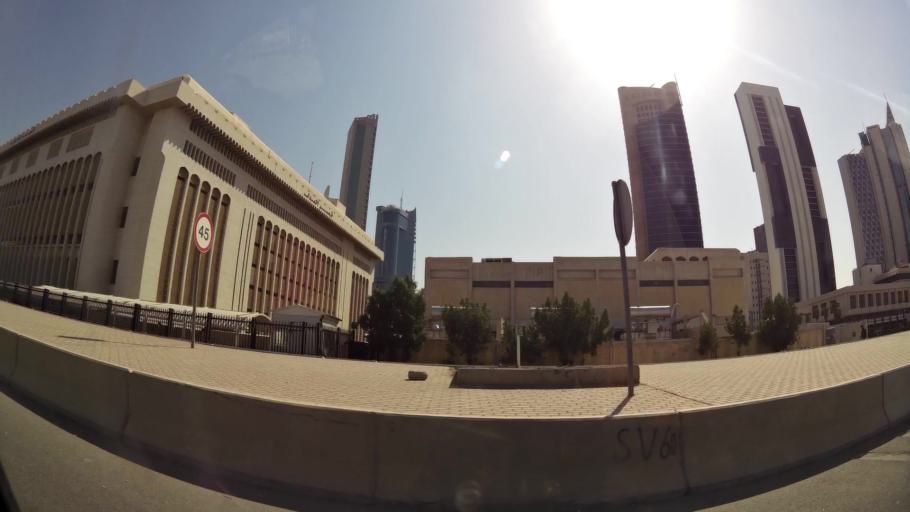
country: KW
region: Al Asimah
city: Kuwait City
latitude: 29.3696
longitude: 47.9662
